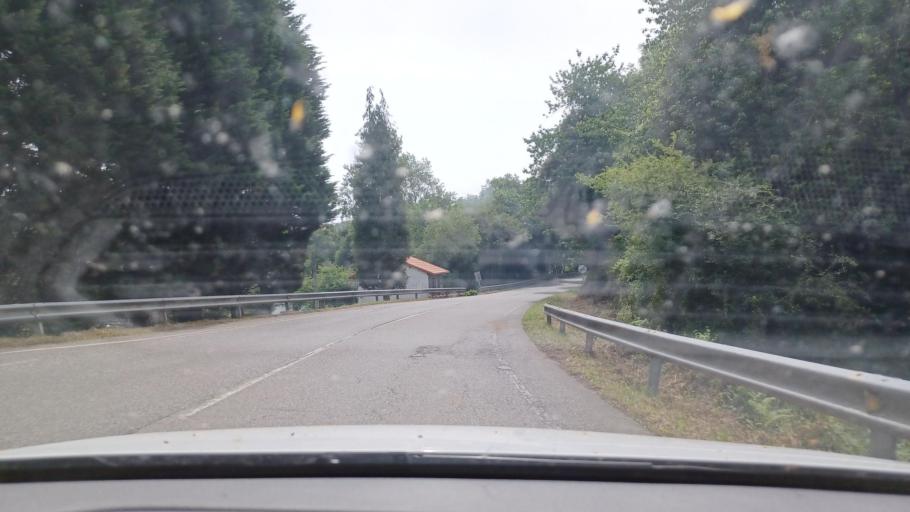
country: ES
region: Asturias
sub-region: Province of Asturias
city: Ribadesella
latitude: 43.4417
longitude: -4.9867
